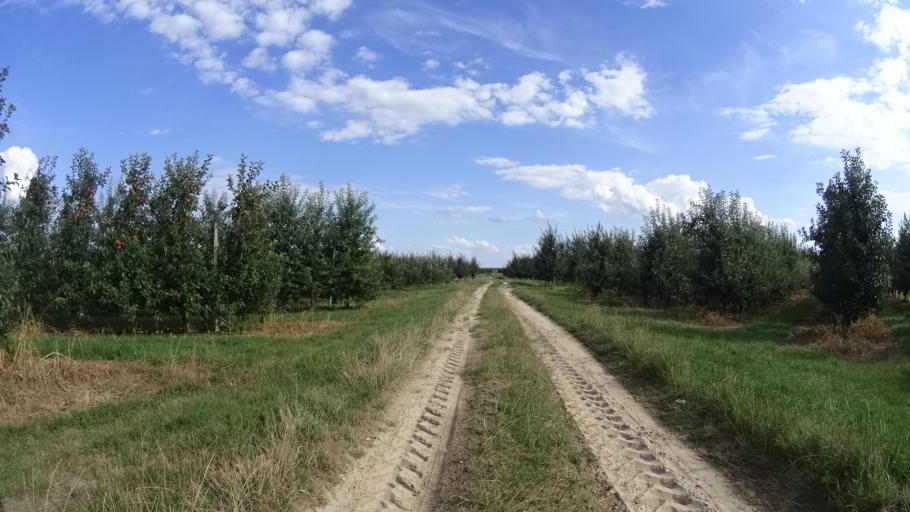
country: PL
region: Masovian Voivodeship
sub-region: Powiat bialobrzeski
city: Wysmierzyce
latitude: 51.6660
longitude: 20.8120
